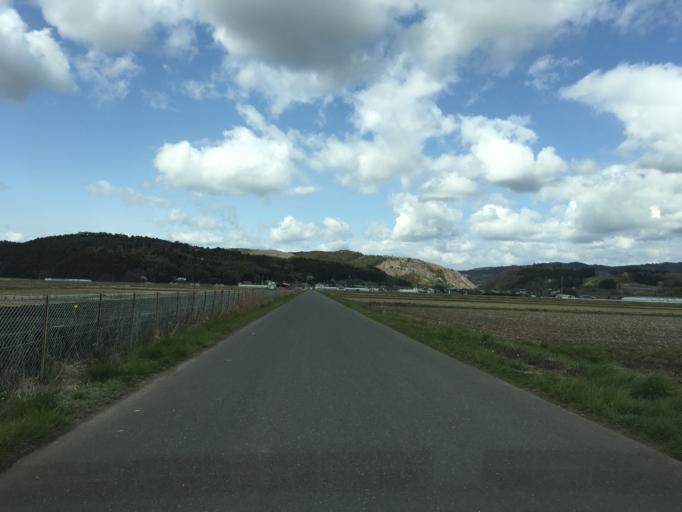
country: JP
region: Iwate
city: Ichinoseki
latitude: 38.7549
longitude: 141.2645
